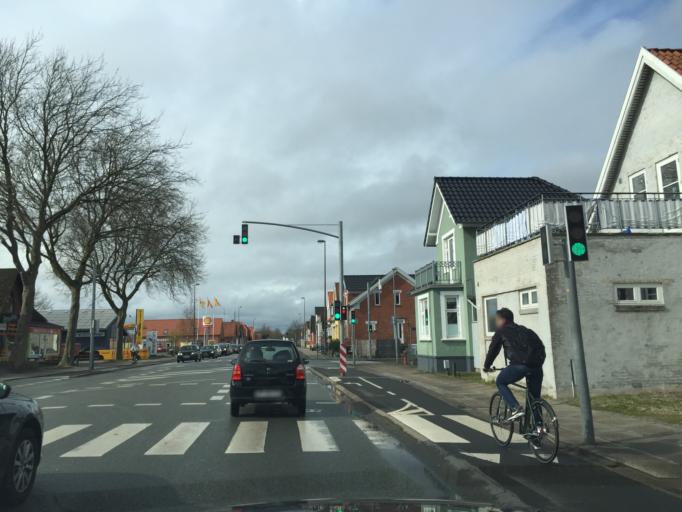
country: DK
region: South Denmark
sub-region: Odense Kommune
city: Odense
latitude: 55.3680
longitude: 10.3726
